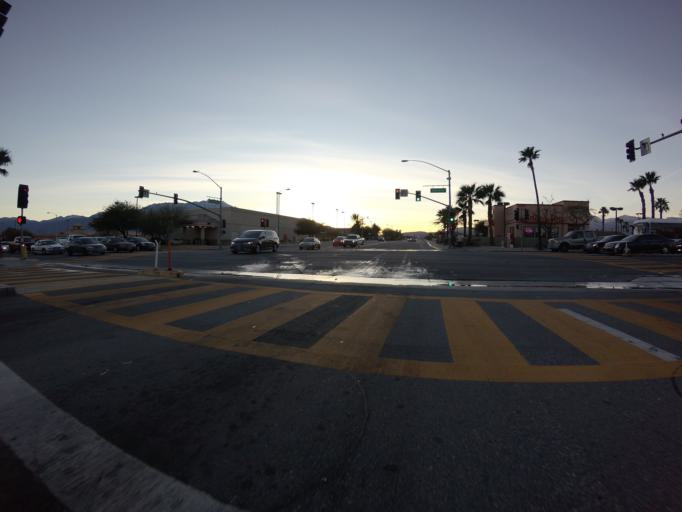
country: US
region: California
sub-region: Riverside County
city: Desert Hot Springs
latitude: 33.9468
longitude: -116.5026
